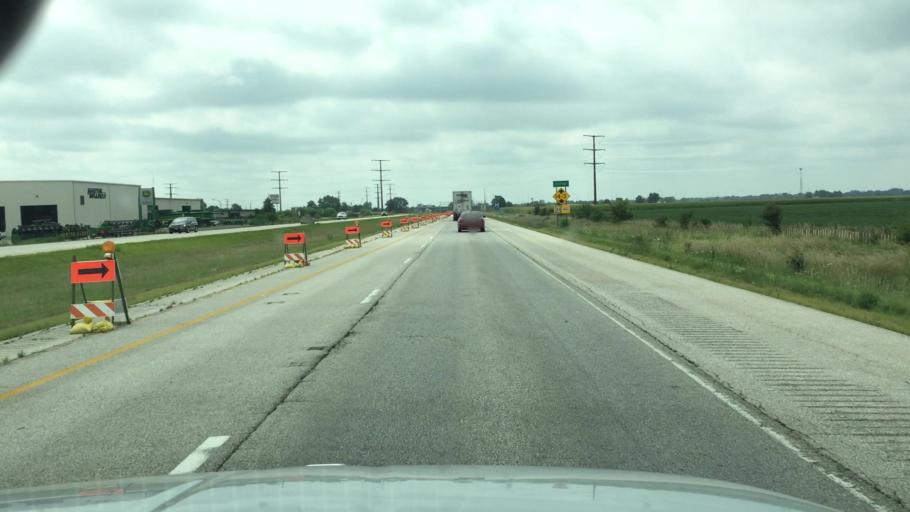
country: US
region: Illinois
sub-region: Knox County
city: Galesburg
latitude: 40.9931
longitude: -90.3361
